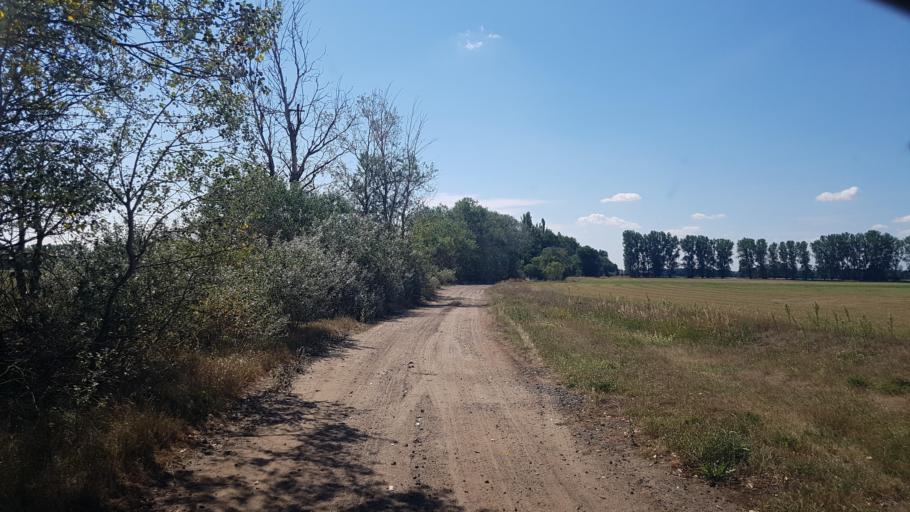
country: DE
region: Brandenburg
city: Golzow
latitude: 52.2505
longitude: 12.6630
